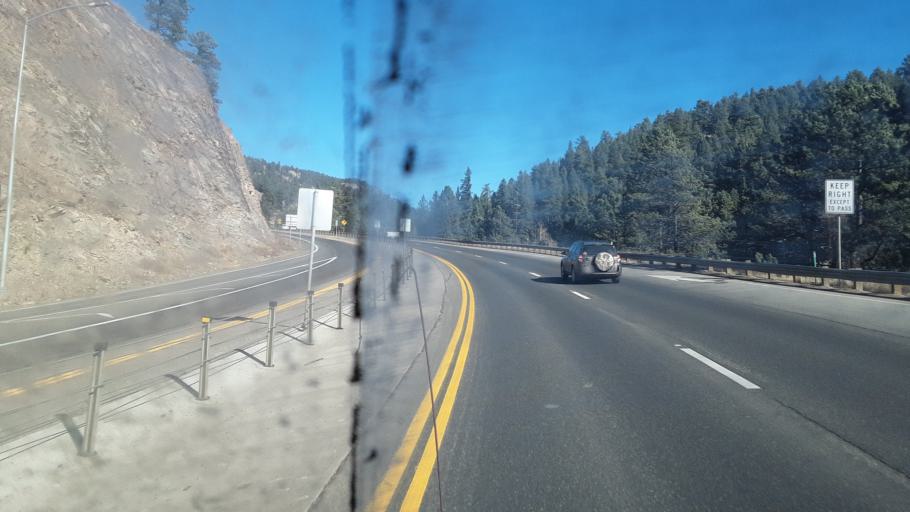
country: US
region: Colorado
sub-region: Jefferson County
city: Evergreen
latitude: 39.4802
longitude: -105.3664
